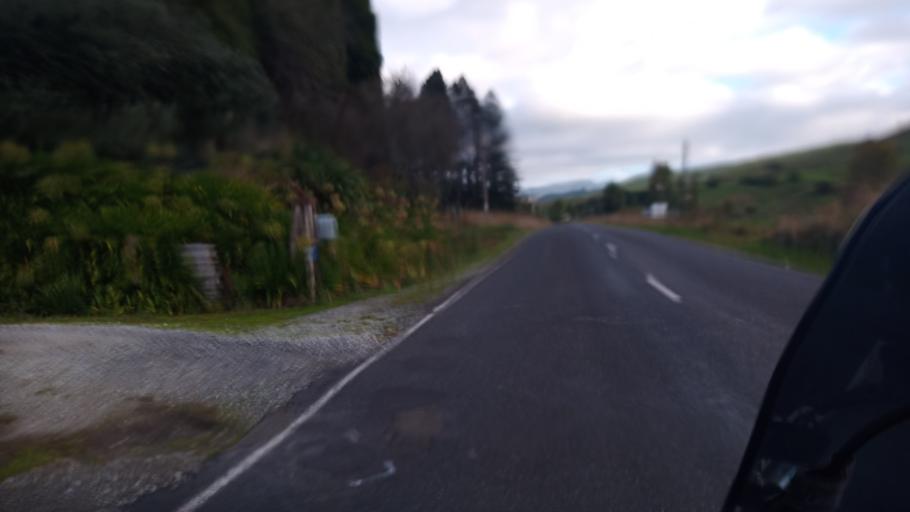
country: NZ
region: Gisborne
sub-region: Gisborne District
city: Gisborne
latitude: -38.5850
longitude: 177.7542
